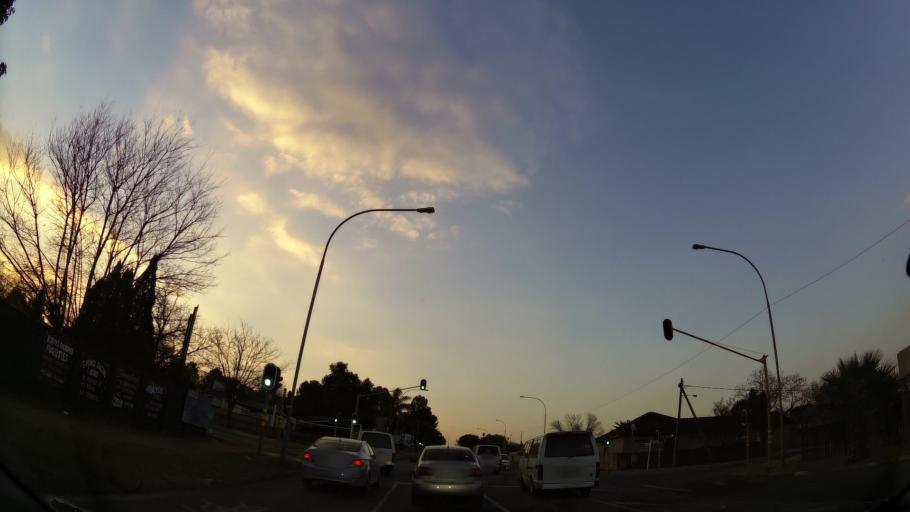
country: ZA
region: Gauteng
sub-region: Ekurhuleni Metropolitan Municipality
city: Benoni
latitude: -26.1774
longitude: 28.3193
